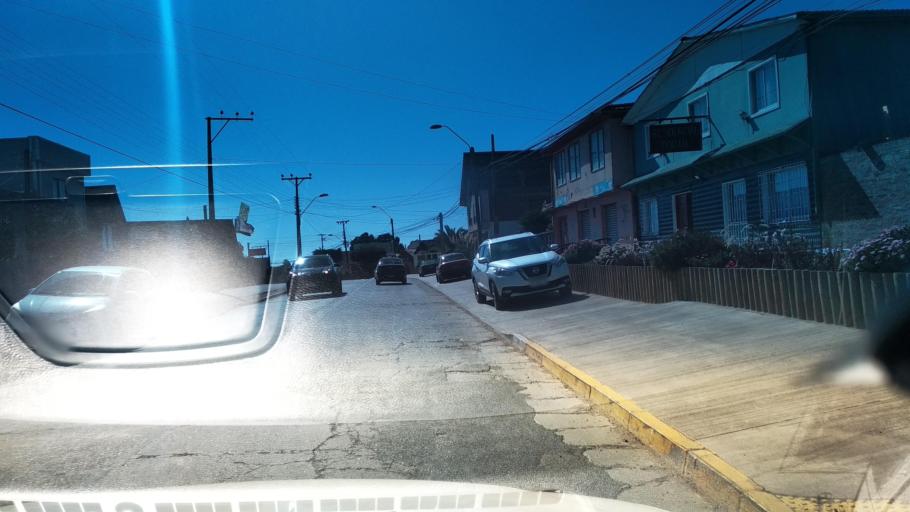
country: CL
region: O'Higgins
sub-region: Provincia de Colchagua
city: Santa Cruz
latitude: -34.3915
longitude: -71.9957
